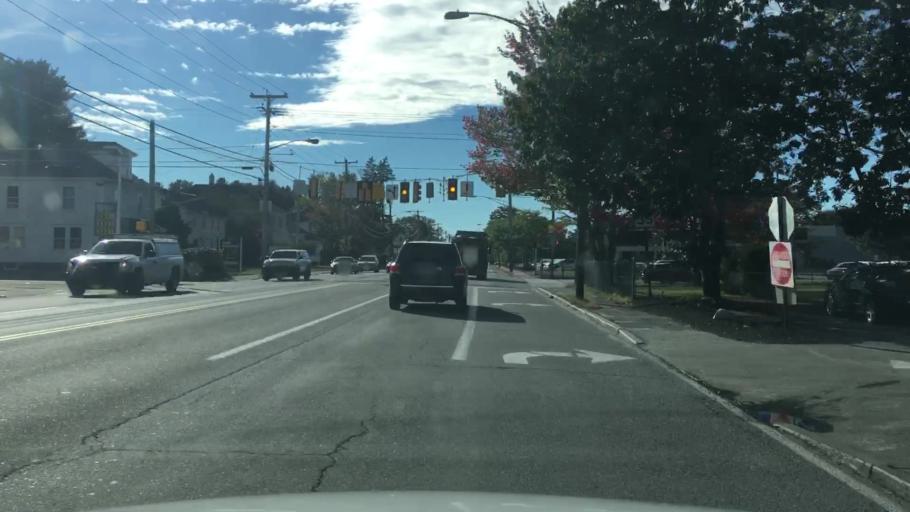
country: US
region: Maine
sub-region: Cumberland County
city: Brunswick
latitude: 43.9129
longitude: -69.9798
